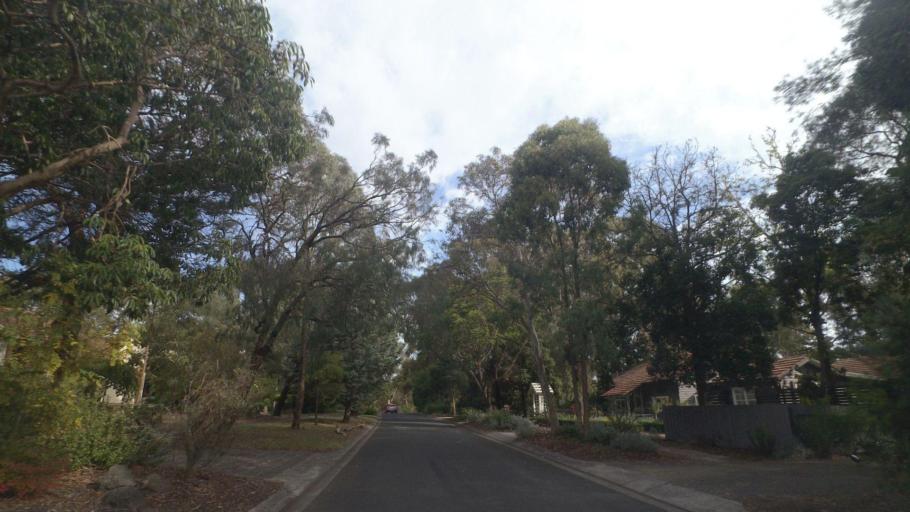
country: AU
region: Victoria
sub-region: Whitehorse
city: Blackburn
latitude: -37.8246
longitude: 145.1428
